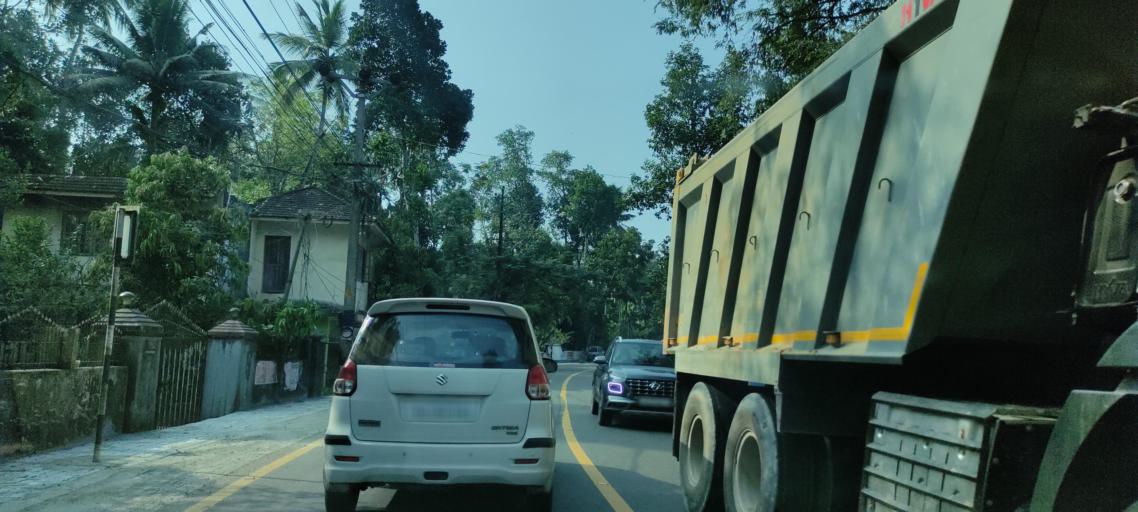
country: IN
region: Kerala
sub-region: Pattanamtitta
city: Tiruvalla
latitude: 9.3685
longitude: 76.5297
